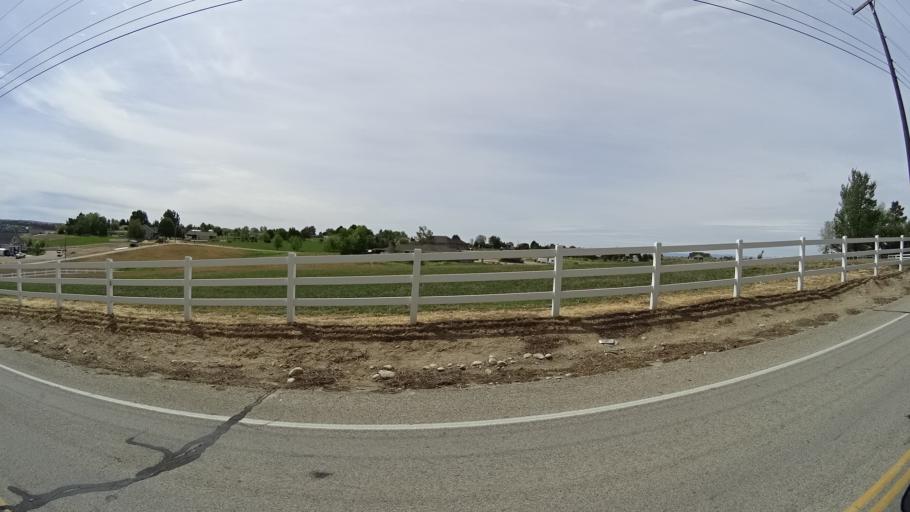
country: US
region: Idaho
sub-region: Ada County
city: Meridian
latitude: 43.5613
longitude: -116.3785
